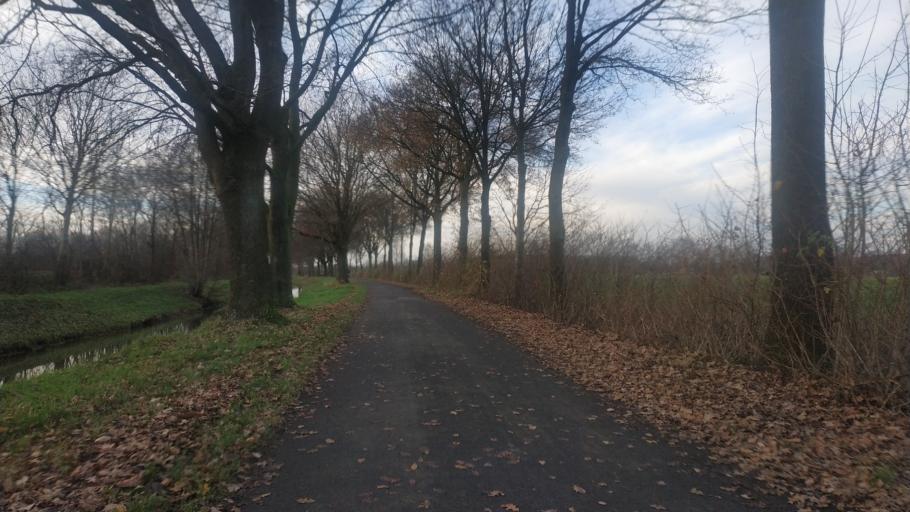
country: DE
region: North Rhine-Westphalia
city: Ibbenburen
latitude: 52.2838
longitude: 7.6773
